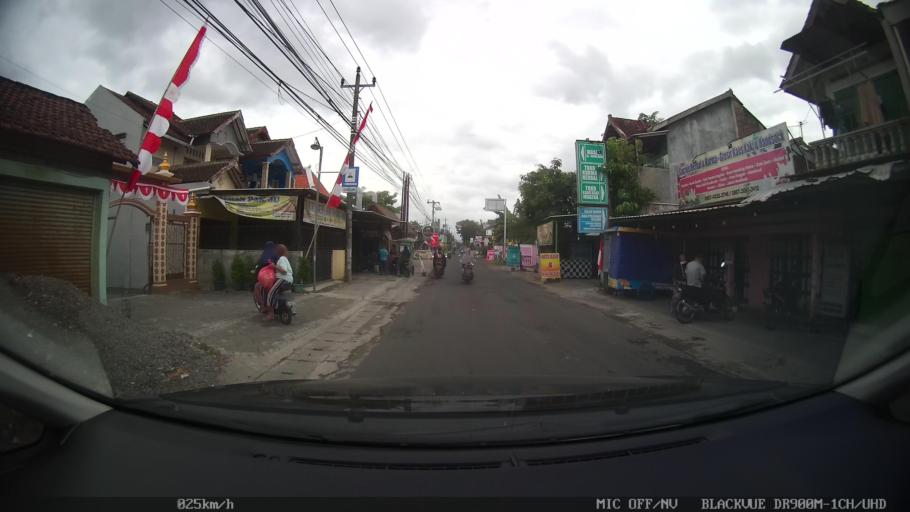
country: ID
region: Daerah Istimewa Yogyakarta
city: Sewon
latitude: -7.8381
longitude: 110.4117
